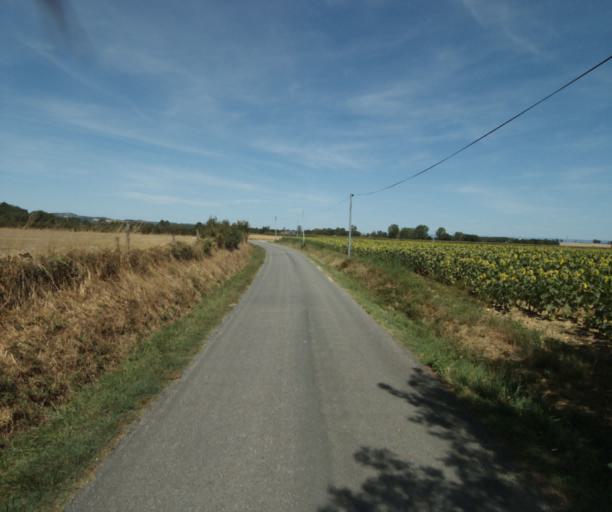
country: FR
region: Midi-Pyrenees
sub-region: Departement de la Haute-Garonne
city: Revel
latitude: 43.5007
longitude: 2.0251
